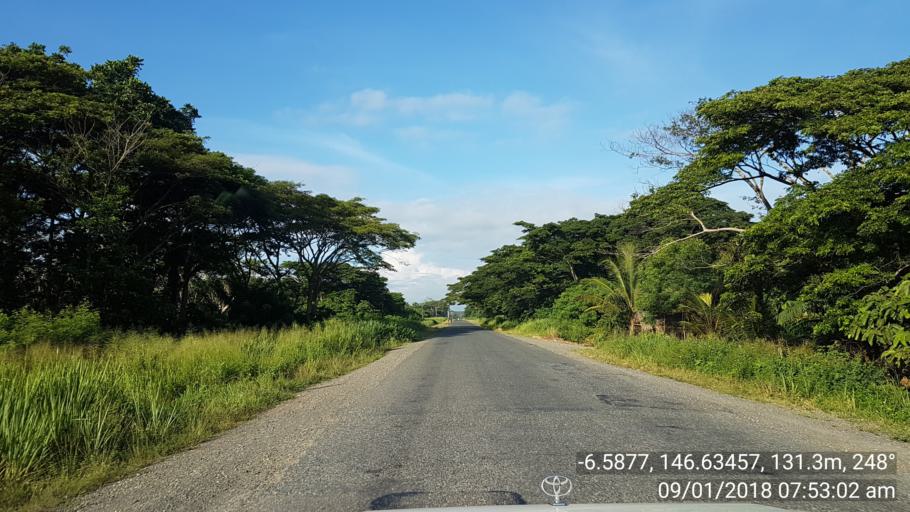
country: PG
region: Morobe
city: Lae
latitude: -6.5878
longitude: 146.6342
